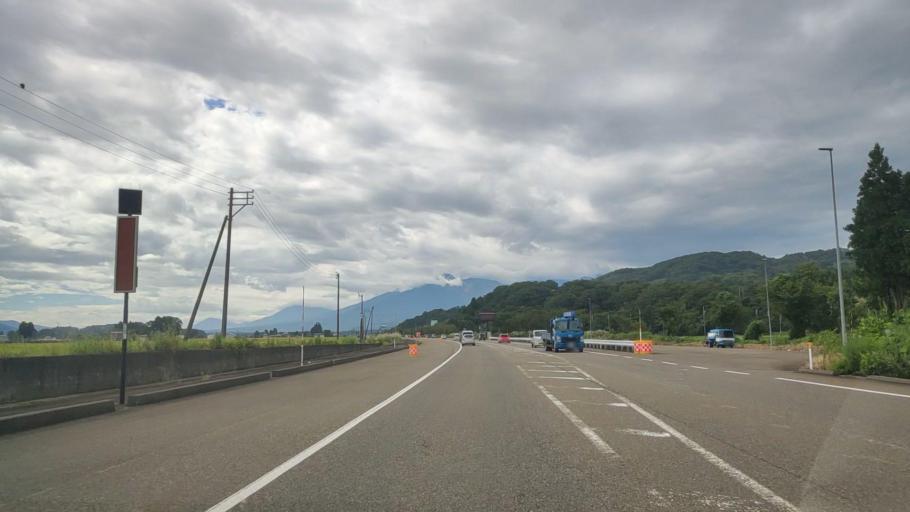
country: JP
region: Niigata
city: Arai
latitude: 37.0457
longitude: 138.2401
